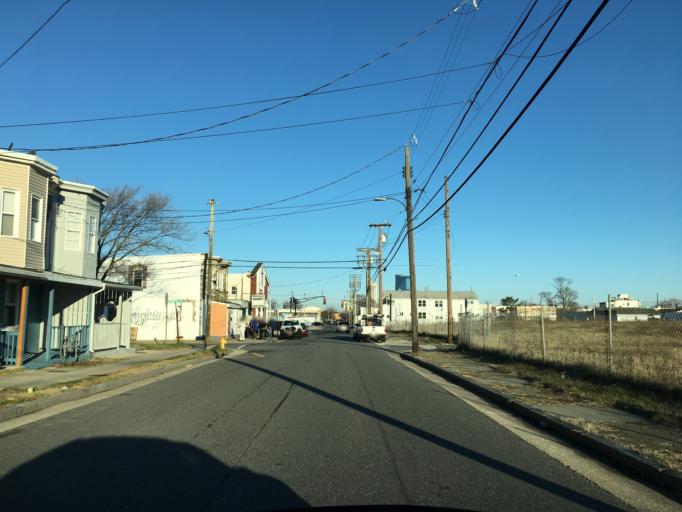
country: US
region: New Jersey
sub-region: Atlantic County
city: Atlantic City
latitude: 39.3689
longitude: -74.4214
